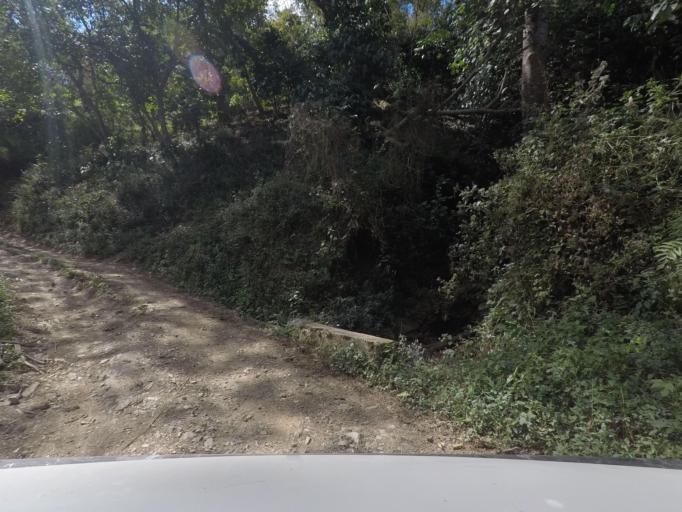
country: TL
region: Ermera
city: Gleno
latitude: -8.7201
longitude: 125.3101
